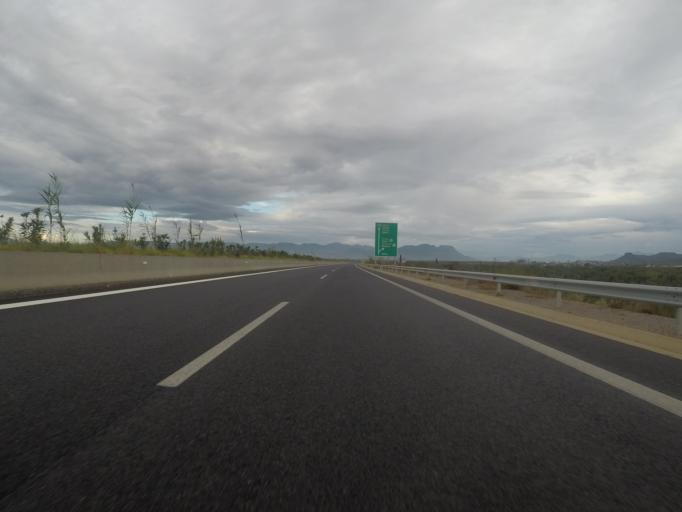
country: GR
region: Peloponnese
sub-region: Nomos Messinias
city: Sperkhoyia
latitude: 37.0656
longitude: 22.0566
